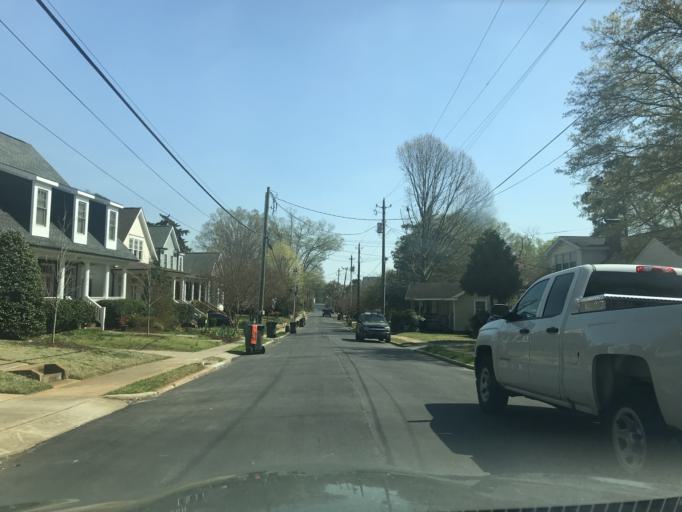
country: US
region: North Carolina
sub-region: Wake County
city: West Raleigh
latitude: 35.8055
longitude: -78.6380
